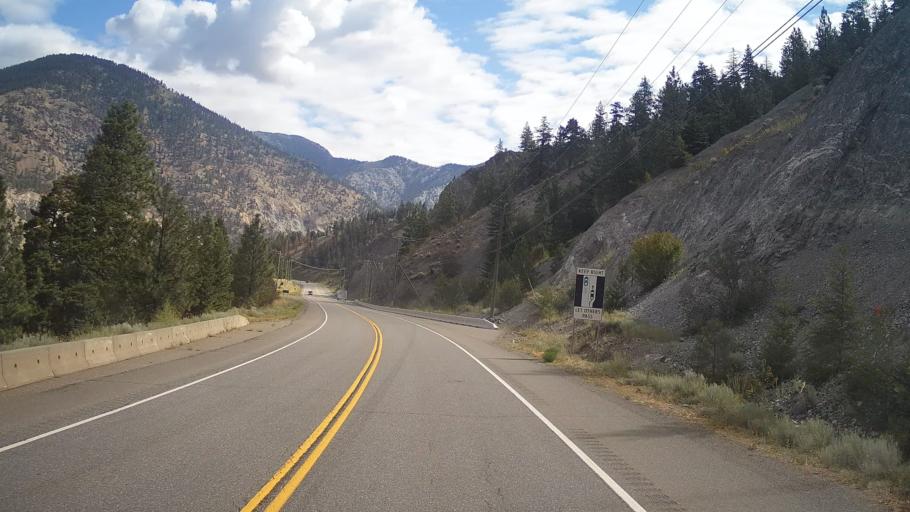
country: CA
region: British Columbia
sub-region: Thompson-Nicola Regional District
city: Ashcroft
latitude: 50.2513
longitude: -121.5497
